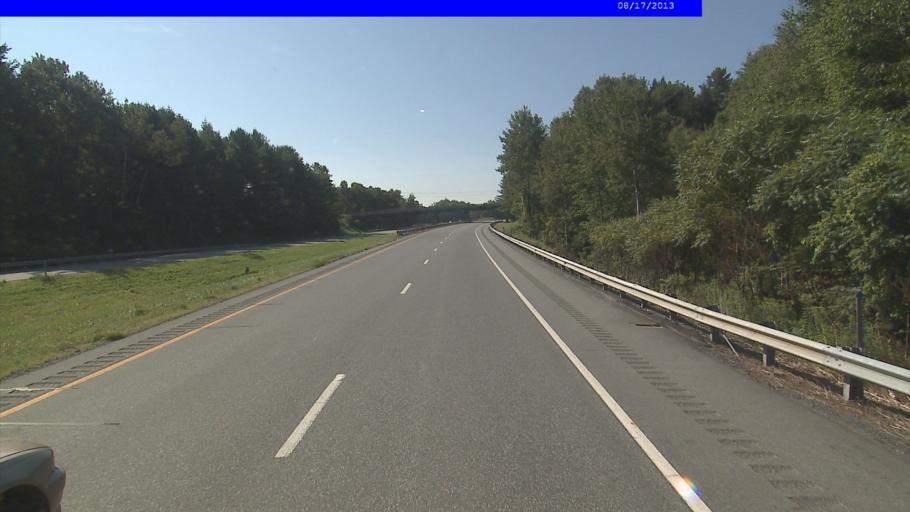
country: US
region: Vermont
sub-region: Windsor County
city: Windsor
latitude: 43.5680
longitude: -72.3860
